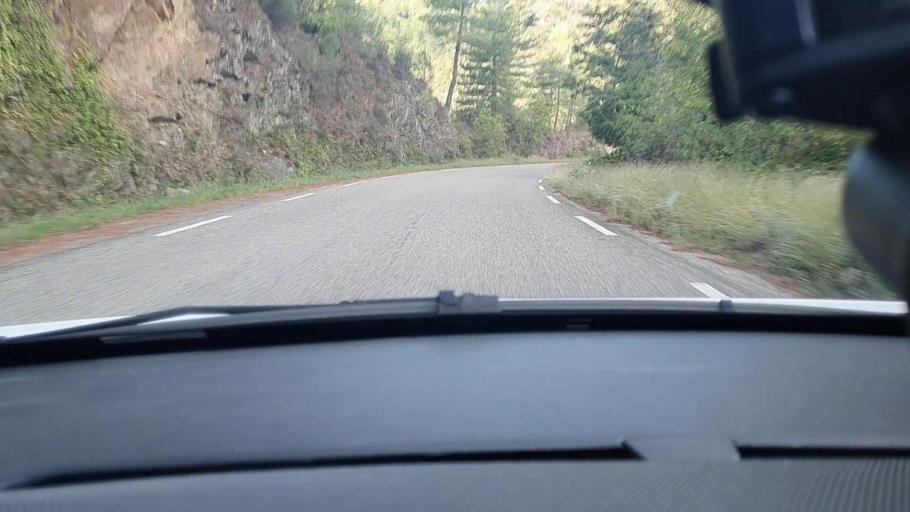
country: FR
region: Languedoc-Roussillon
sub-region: Departement du Gard
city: Besseges
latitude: 44.3176
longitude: 4.0392
